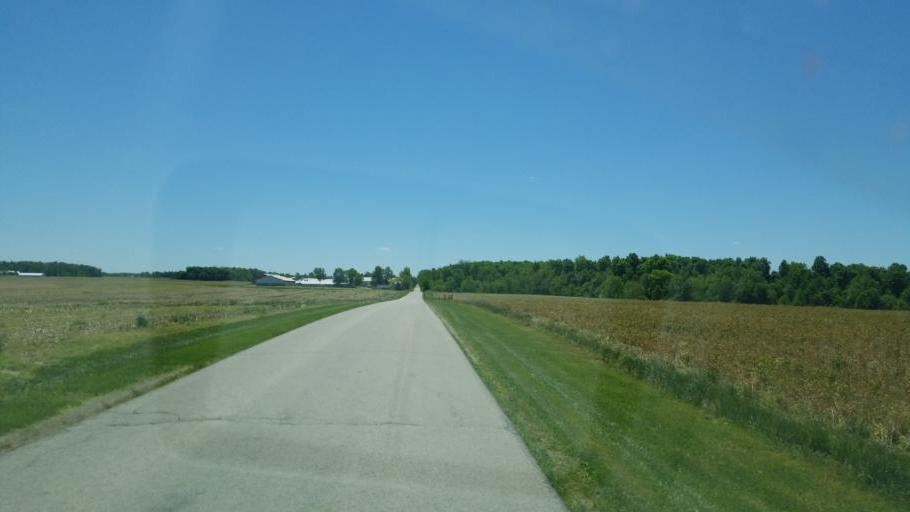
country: US
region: Ohio
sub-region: Mercer County
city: Fort Recovery
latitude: 40.3611
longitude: -84.8040
